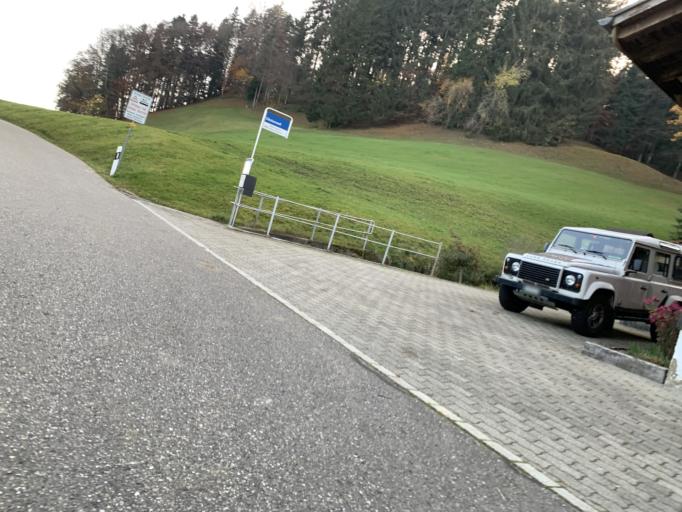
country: CH
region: Zurich
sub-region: Bezirk Hinwil
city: Wald
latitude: 47.2876
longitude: 8.9071
